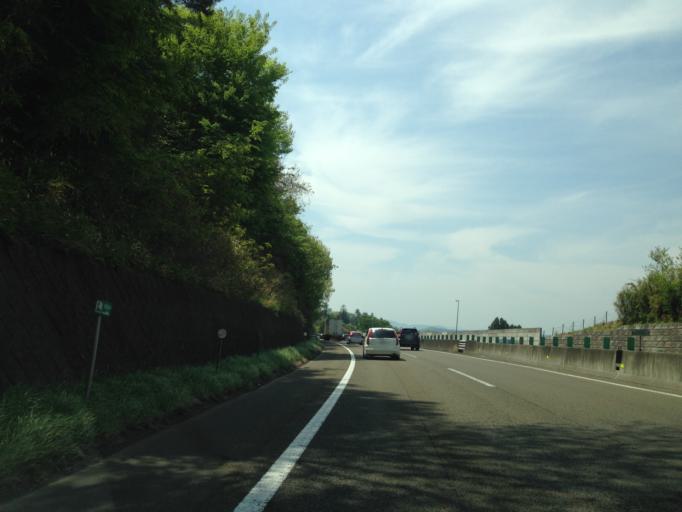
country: JP
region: Miyagi
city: Okawara
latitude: 38.0979
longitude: 140.6849
